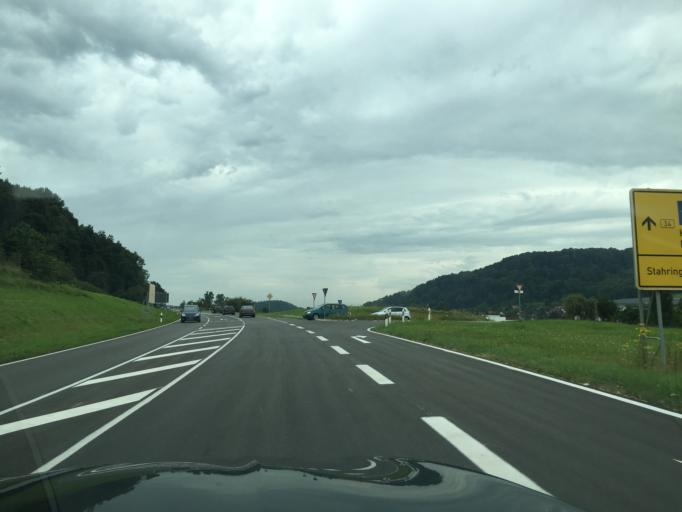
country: DE
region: Baden-Wuerttemberg
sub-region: Freiburg Region
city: Steisslingen
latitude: 47.7948
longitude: 8.9813
